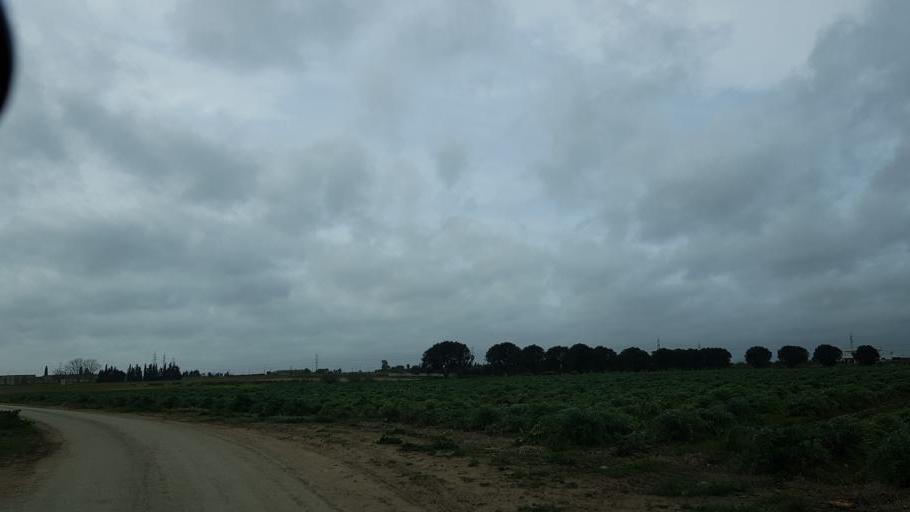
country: IT
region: Apulia
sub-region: Provincia di Brindisi
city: La Rosa
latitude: 40.5960
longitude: 17.9181
